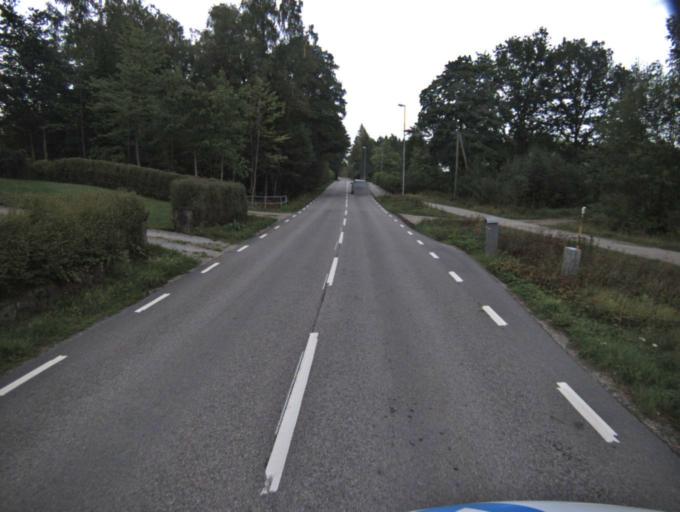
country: SE
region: Vaestra Goetaland
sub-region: Ulricehamns Kommun
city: Ulricehamn
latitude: 57.7773
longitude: 13.4265
